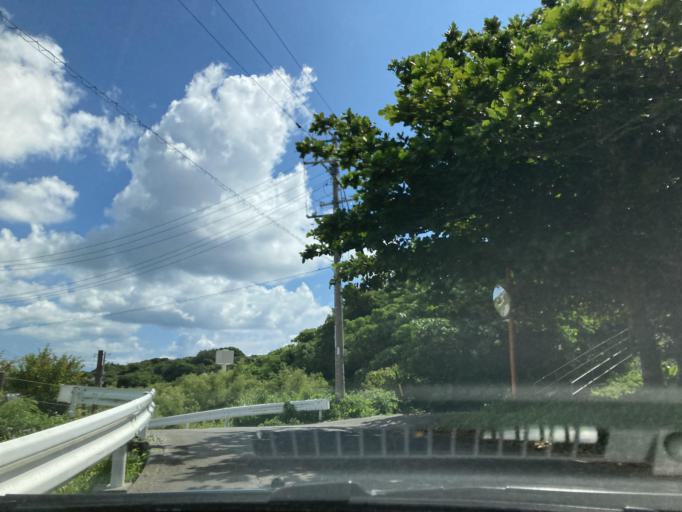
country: JP
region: Okinawa
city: Itoman
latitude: 26.1204
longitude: 127.7438
